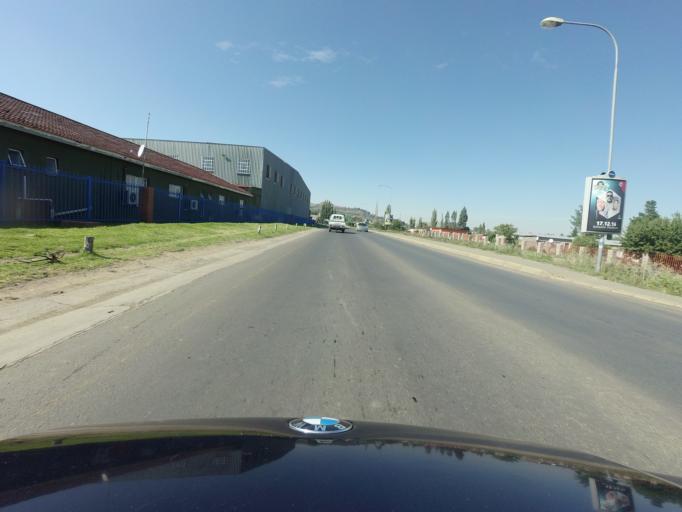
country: LS
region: Maseru
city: Maseru
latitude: -29.3038
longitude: 27.5006
